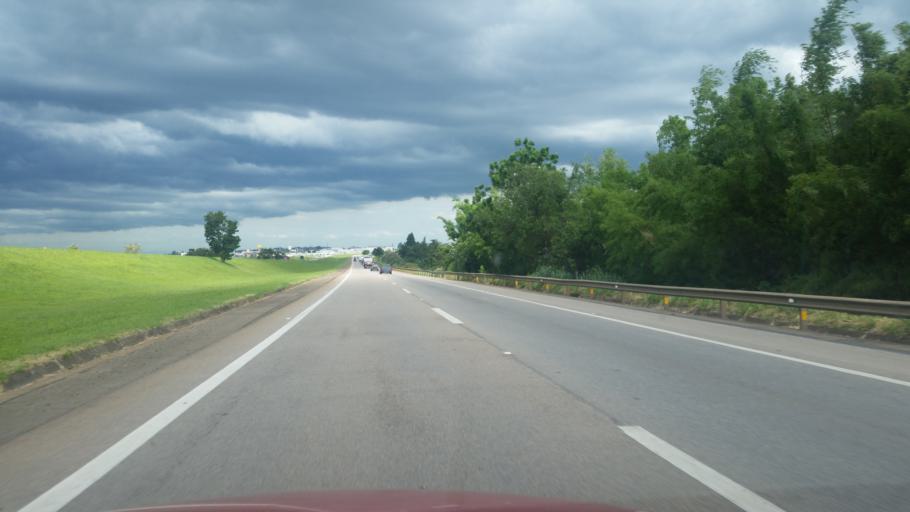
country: BR
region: Sao Paulo
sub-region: Boituva
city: Boituva
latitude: -23.2986
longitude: -47.6760
